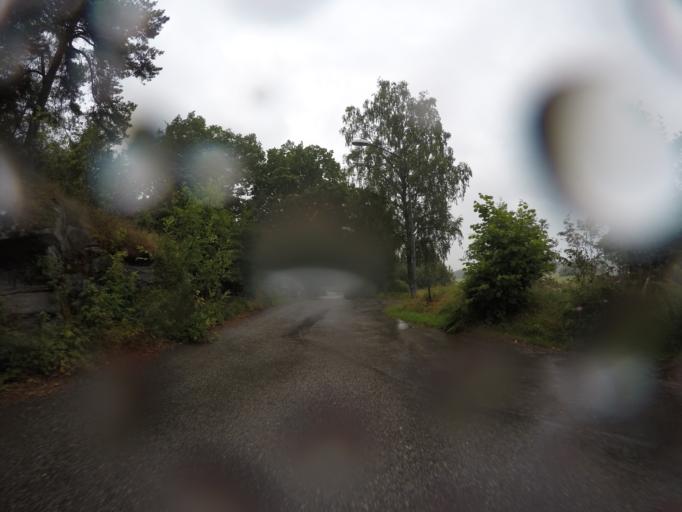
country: SE
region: Vaestra Goetaland
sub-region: Trollhattan
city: Sjuntorp
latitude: 58.1621
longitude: 12.3045
